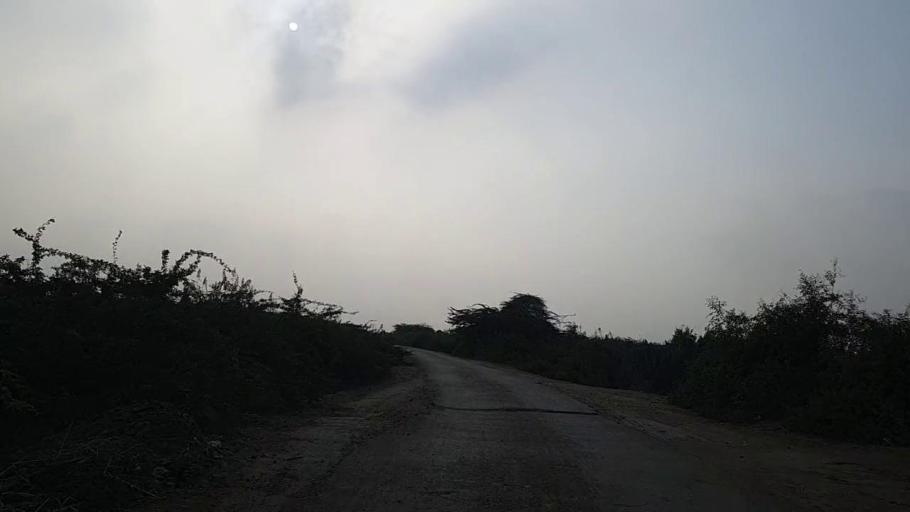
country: PK
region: Sindh
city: Mirpur Sakro
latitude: 24.6139
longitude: 67.5405
